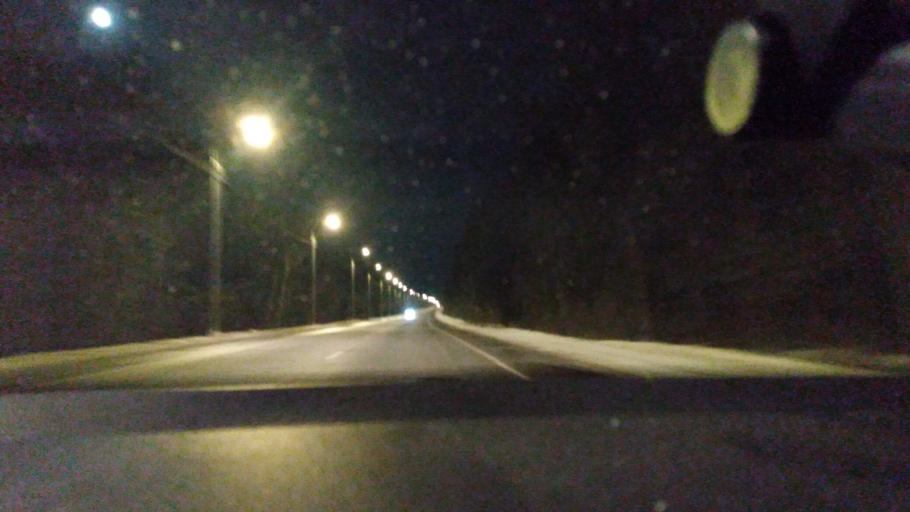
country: RU
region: Moskovskaya
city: Il'inskiy Pogost
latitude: 55.4740
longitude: 38.9547
